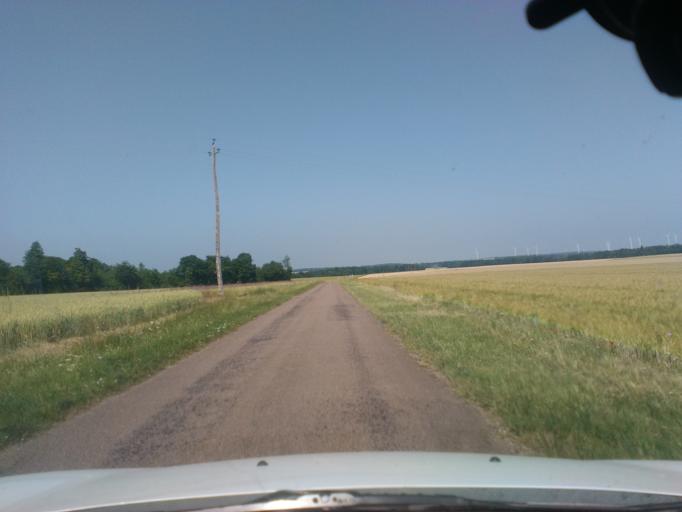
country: FR
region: Lorraine
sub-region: Departement des Vosges
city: Liffol-le-Grand
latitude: 48.3037
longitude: 5.4451
